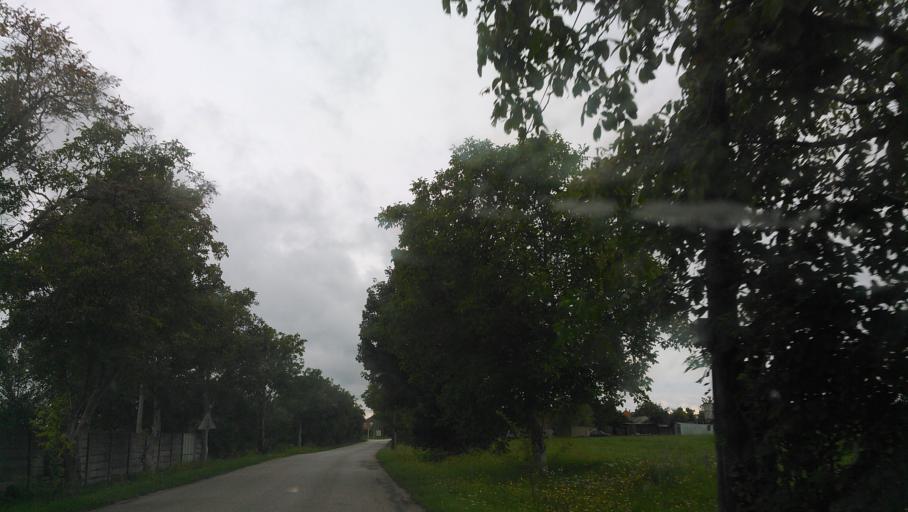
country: SK
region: Trnavsky
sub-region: Okres Dunajska Streda
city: Velky Meder
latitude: 47.8818
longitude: 17.8164
